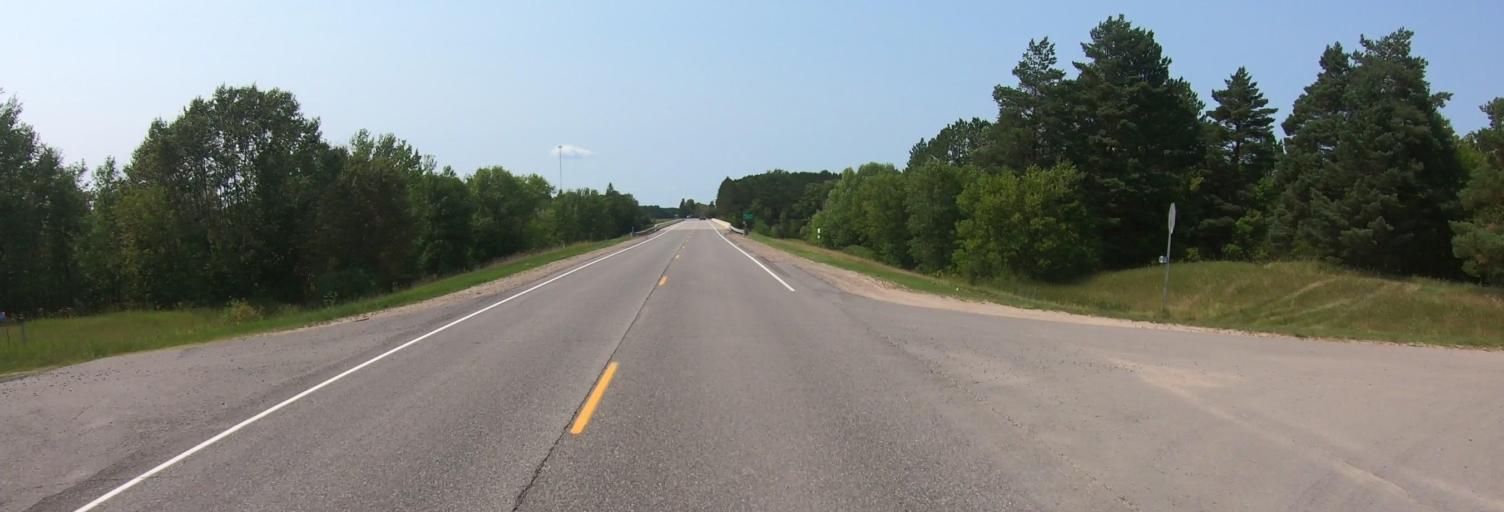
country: US
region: Minnesota
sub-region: Koochiching County
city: International Falls
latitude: 48.5217
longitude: -93.5839
